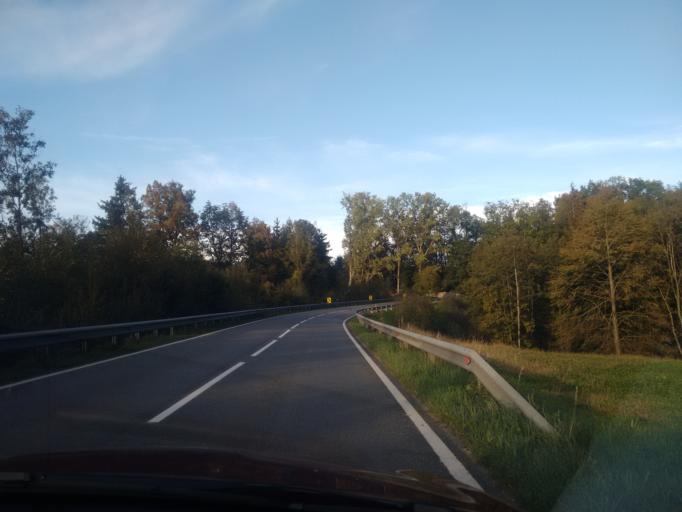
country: AT
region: Upper Austria
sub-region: Politischer Bezirk Vocklabruck
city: Niederthalheim
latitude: 48.1559
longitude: 13.7361
